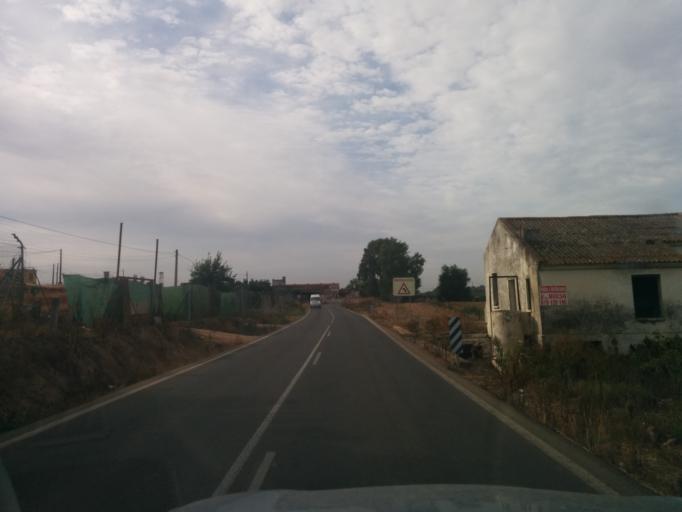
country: ES
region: Andalusia
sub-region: Provincia de Sevilla
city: La Algaba
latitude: 37.5017
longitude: -6.0241
